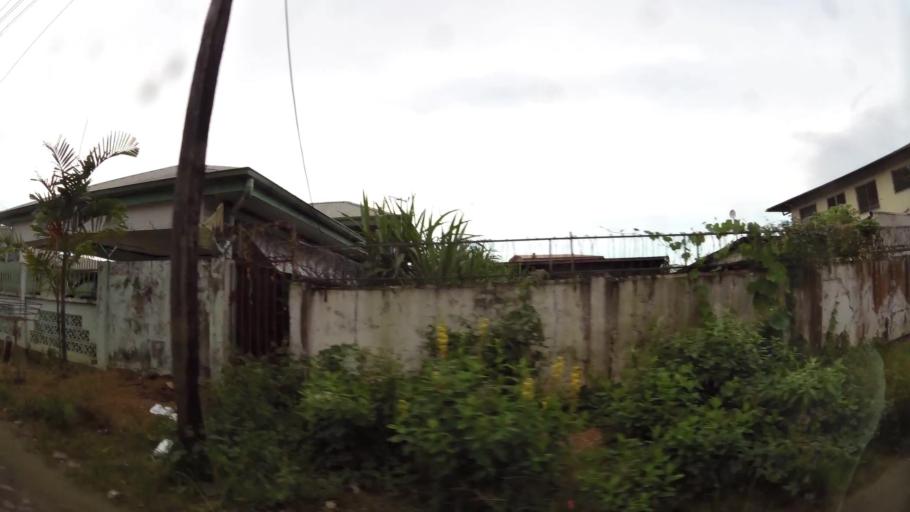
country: SR
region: Paramaribo
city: Paramaribo
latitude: 5.8271
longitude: -55.1999
